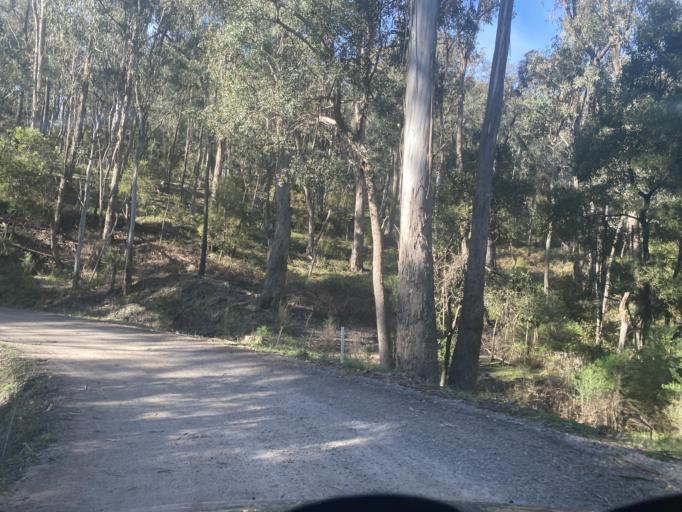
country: AU
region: Victoria
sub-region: Mansfield
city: Mansfield
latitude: -36.8244
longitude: 146.1534
